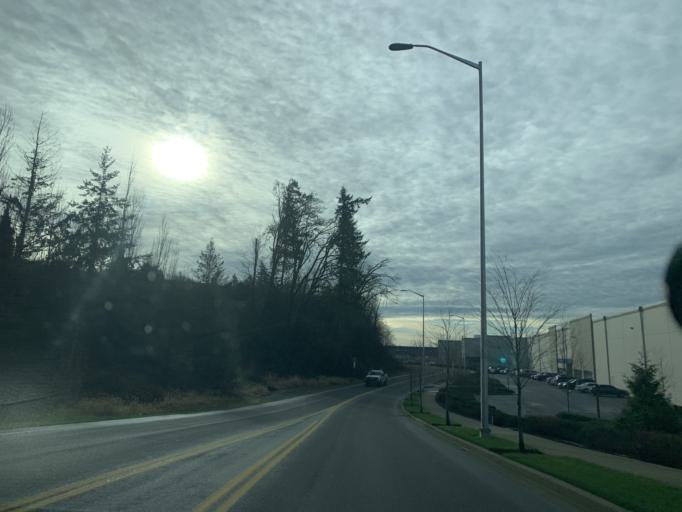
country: US
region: Washington
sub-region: Pierce County
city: Milton
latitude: 47.2334
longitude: -122.3239
